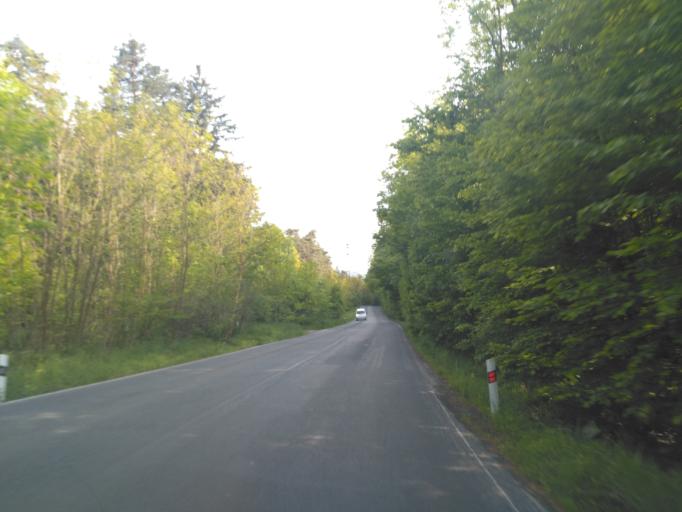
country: CZ
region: Central Bohemia
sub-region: Okres Beroun
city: Beroun
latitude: 49.9882
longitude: 14.0860
